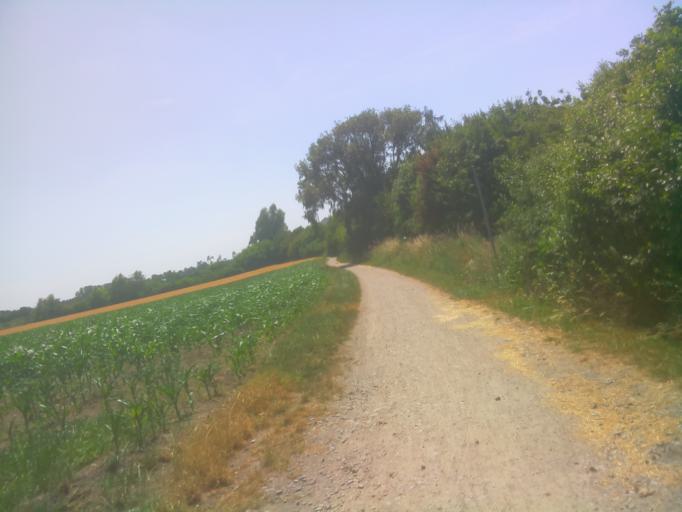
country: DE
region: Hesse
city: Lorsch
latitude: 49.6434
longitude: 8.5751
